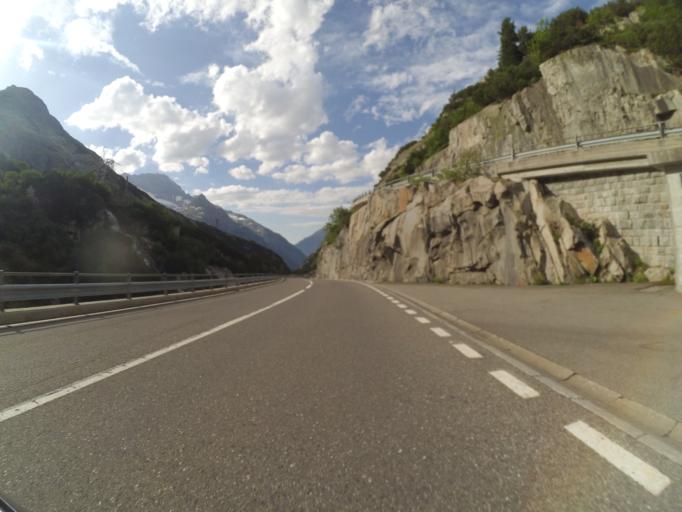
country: CH
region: Bern
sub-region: Interlaken-Oberhasli District
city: Meiringen
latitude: 46.5914
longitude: 8.3245
